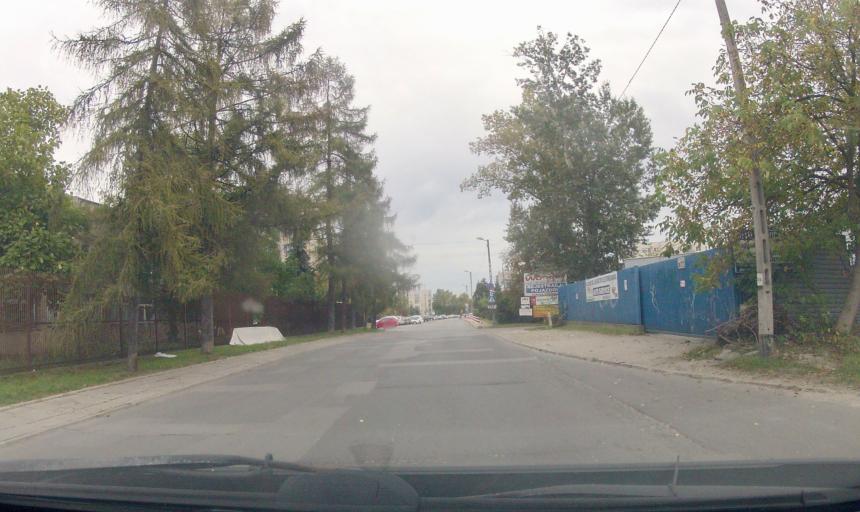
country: PL
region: Lesser Poland Voivodeship
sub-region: Krakow
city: Krakow
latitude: 50.0451
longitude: 19.9964
